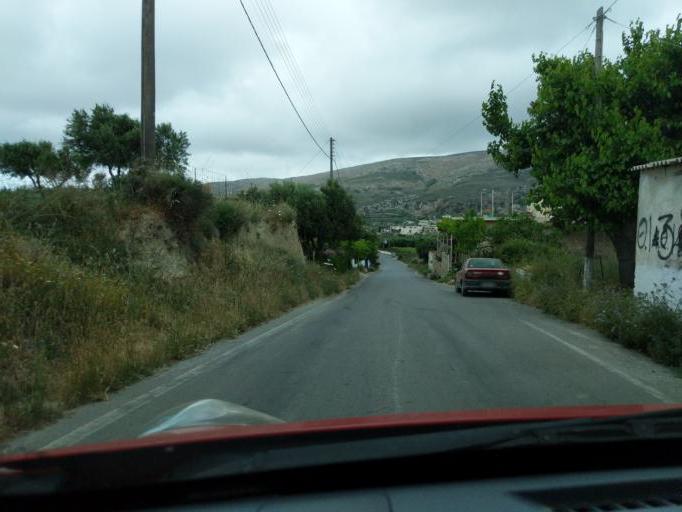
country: GR
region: Crete
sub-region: Nomos Chanias
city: Platanos
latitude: 35.4751
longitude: 23.5946
